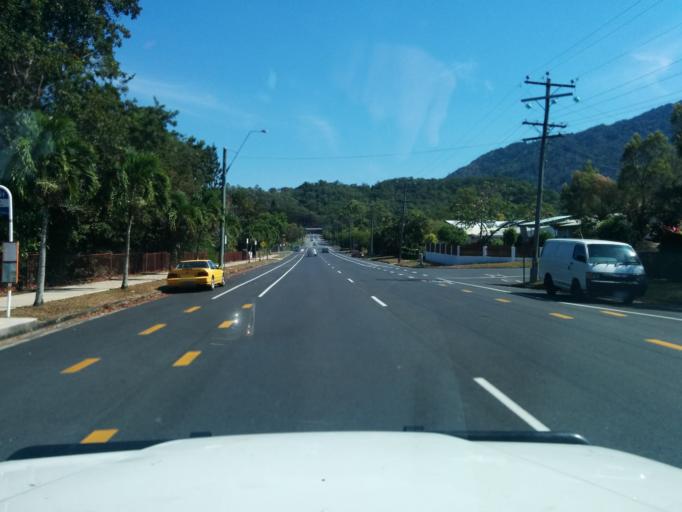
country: AU
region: Queensland
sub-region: Cairns
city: Redlynch
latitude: -16.9083
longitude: 145.7284
